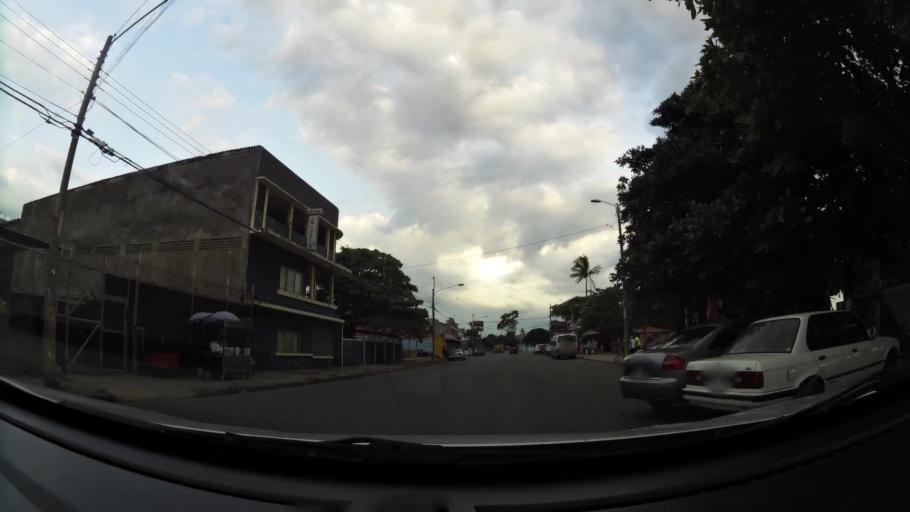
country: CR
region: Puntarenas
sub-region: Canton Central de Puntarenas
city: Puntarenas
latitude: 9.9751
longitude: -84.8349
